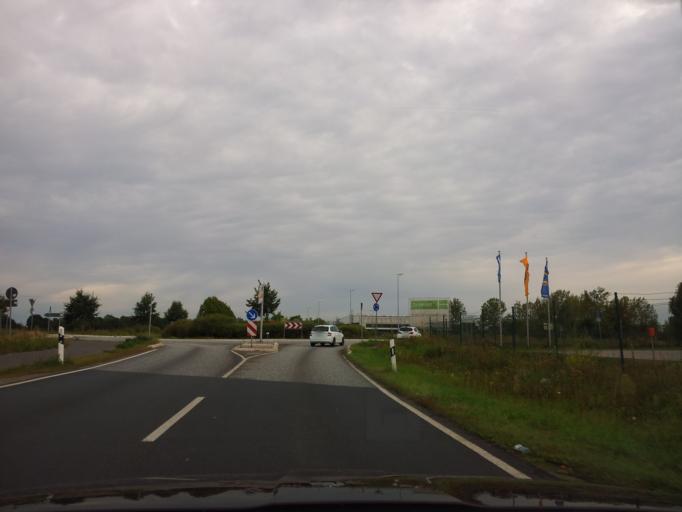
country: DE
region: Brandenburg
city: Ludwigsfelde
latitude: 52.3150
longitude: 13.2832
